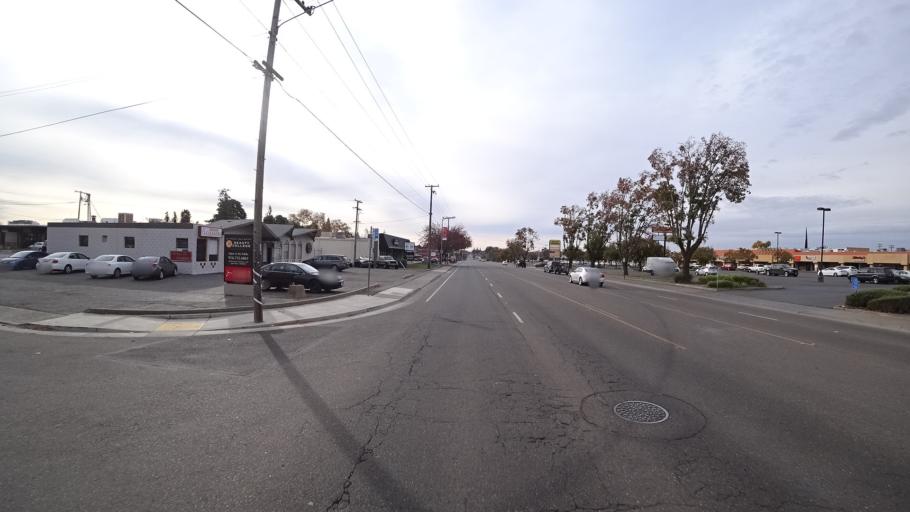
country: US
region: California
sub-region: Sacramento County
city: Citrus Heights
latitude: 38.7133
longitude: -121.2903
